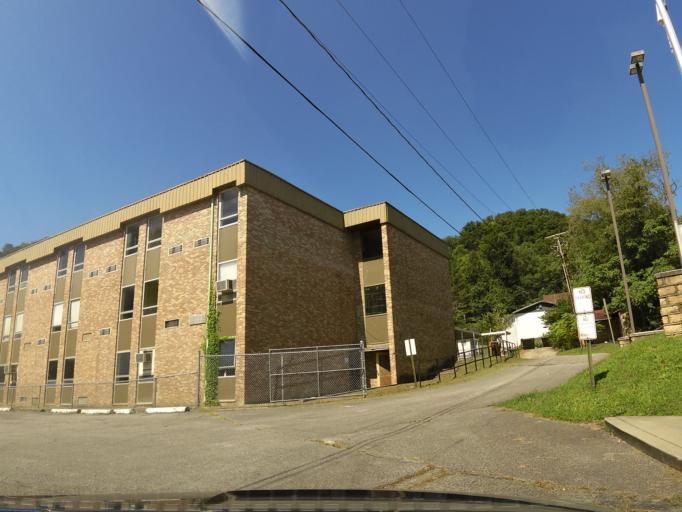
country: US
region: Kentucky
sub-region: Leslie County
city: Hyden
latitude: 37.1636
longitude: -83.3767
